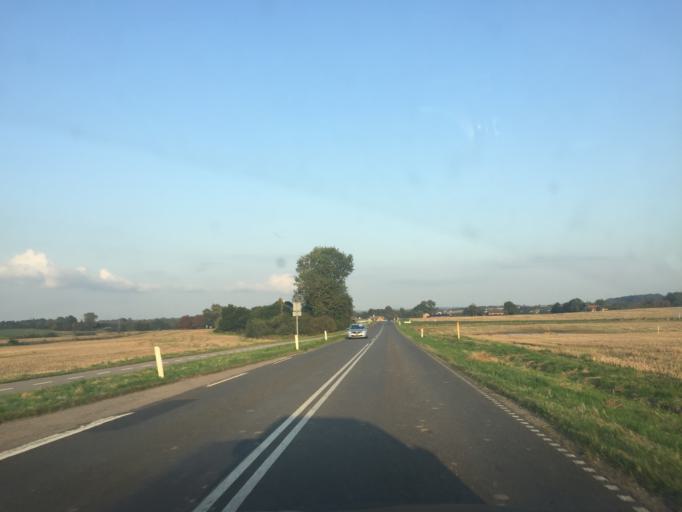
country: DK
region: Zealand
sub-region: Soro Kommune
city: Stenlille
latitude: 55.5426
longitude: 11.6676
